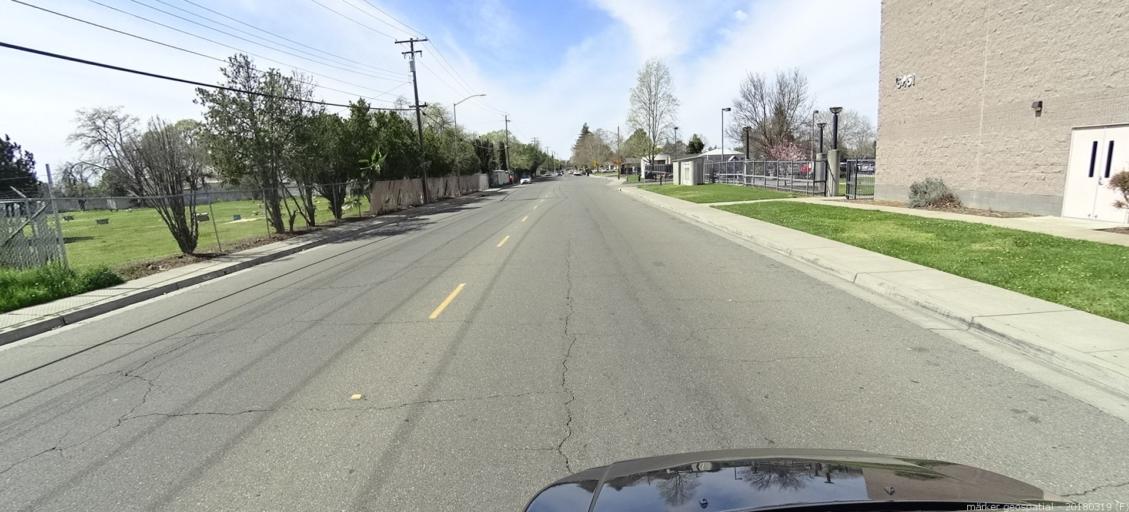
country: US
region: California
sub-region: Sacramento County
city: Parkway
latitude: 38.5158
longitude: -121.4406
